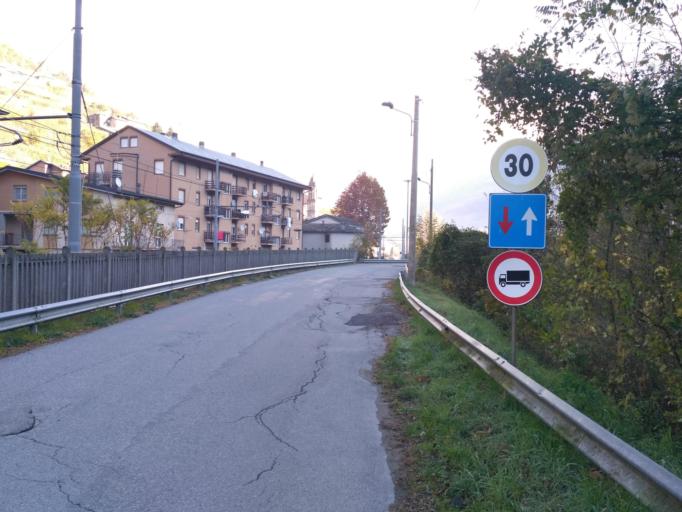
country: IT
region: Lombardy
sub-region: Provincia di Sondrio
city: Teglio
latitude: 46.1621
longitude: 10.0839
